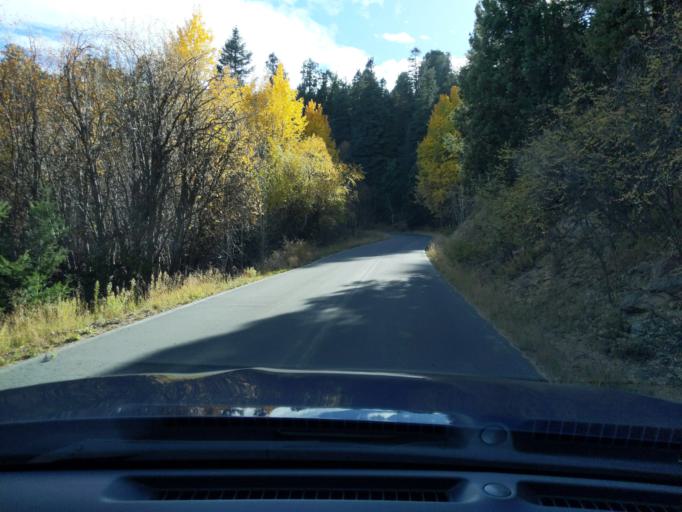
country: US
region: Arizona
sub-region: Pima County
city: Catalina
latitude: 32.4433
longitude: -110.7865
